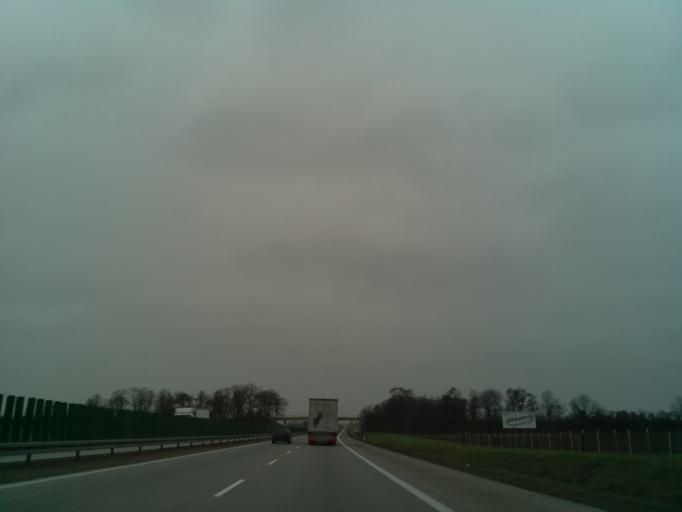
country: PL
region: Lower Silesian Voivodeship
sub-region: Powiat wroclawski
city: Smolec
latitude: 51.0351
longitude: 16.8588
